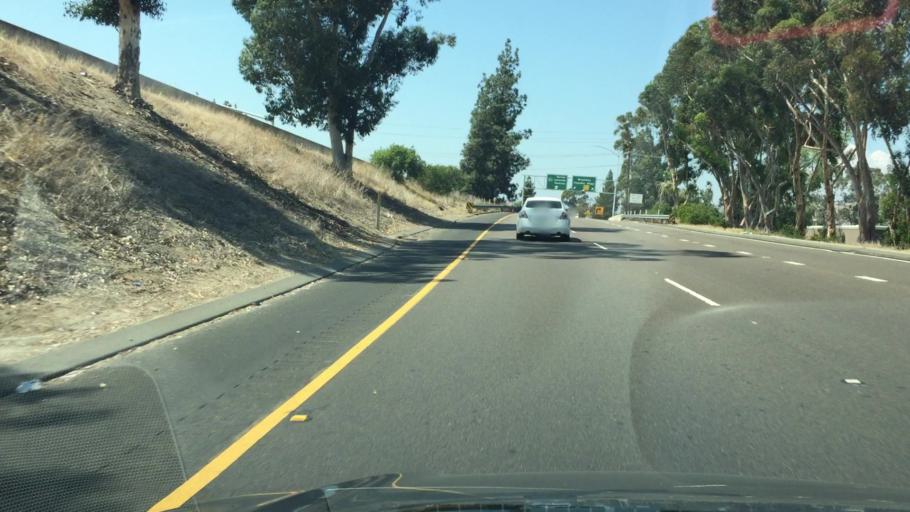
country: US
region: California
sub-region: San Diego County
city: El Cajon
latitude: 32.8063
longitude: -116.9617
